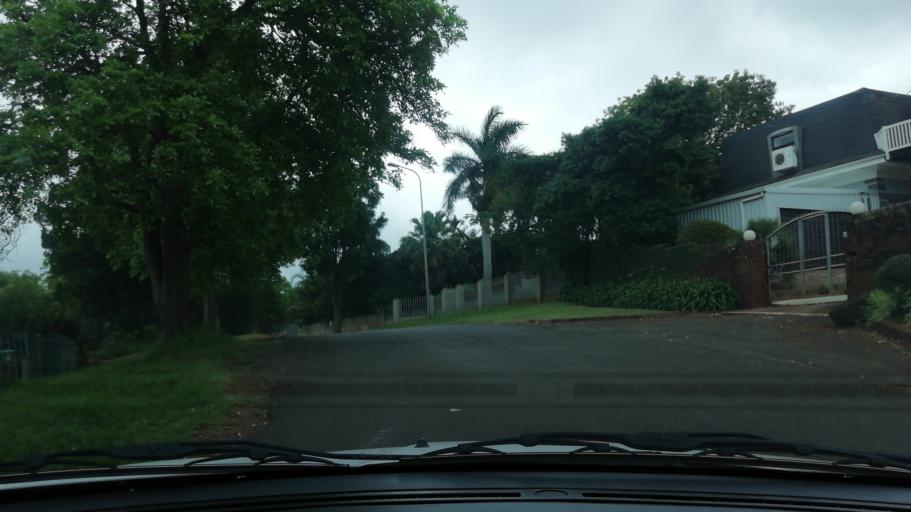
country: ZA
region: KwaZulu-Natal
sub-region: uThungulu District Municipality
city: Empangeni
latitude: -28.7655
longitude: 31.8939
